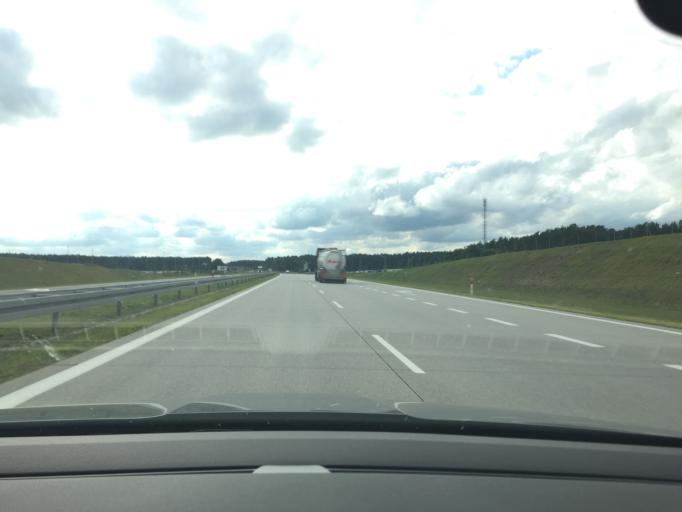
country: PL
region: Lubusz
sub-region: Powiat sulecinski
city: Torzym
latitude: 52.3248
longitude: 15.1699
